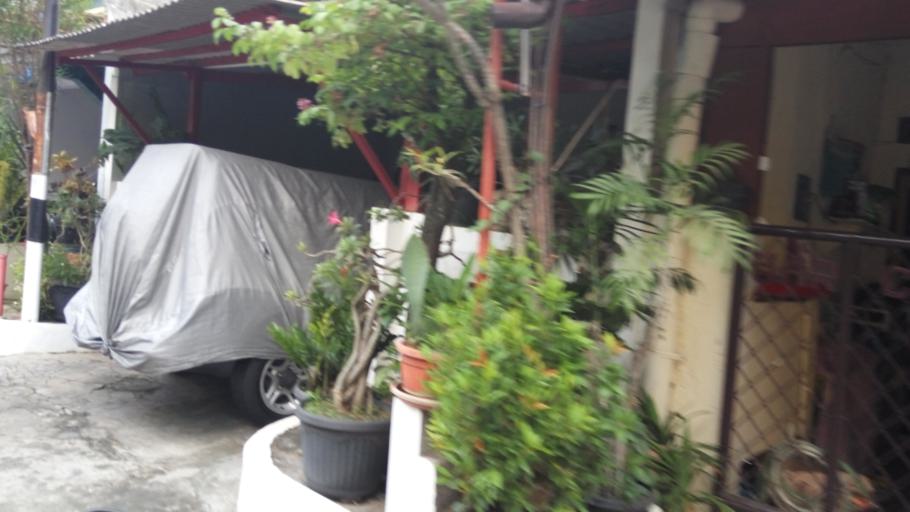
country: ID
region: Central Java
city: Mranggen
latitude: -7.0364
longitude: 110.4705
